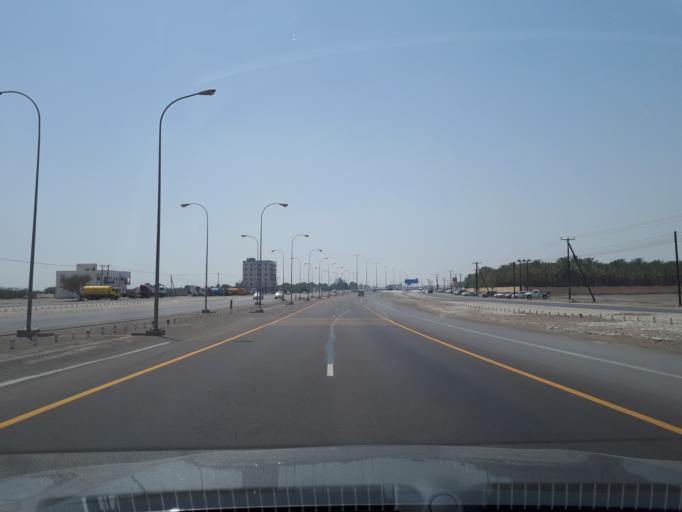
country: OM
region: Al Batinah
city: Al Sohar
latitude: 24.4135
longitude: 56.6332
